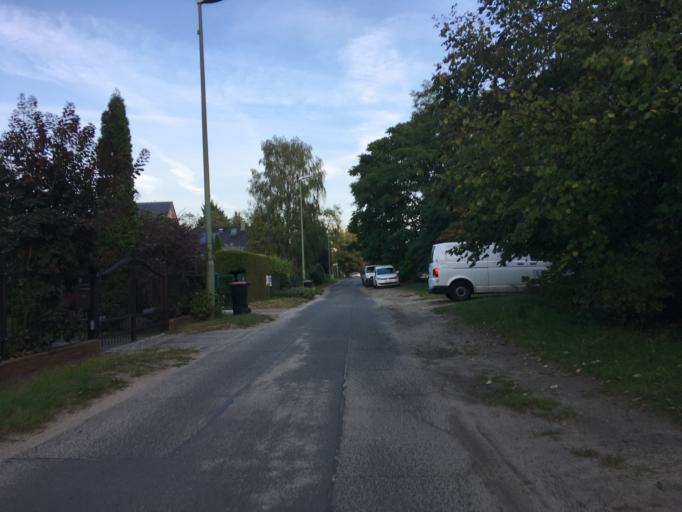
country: DE
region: Berlin
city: Biesdorf
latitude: 52.4929
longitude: 13.5509
